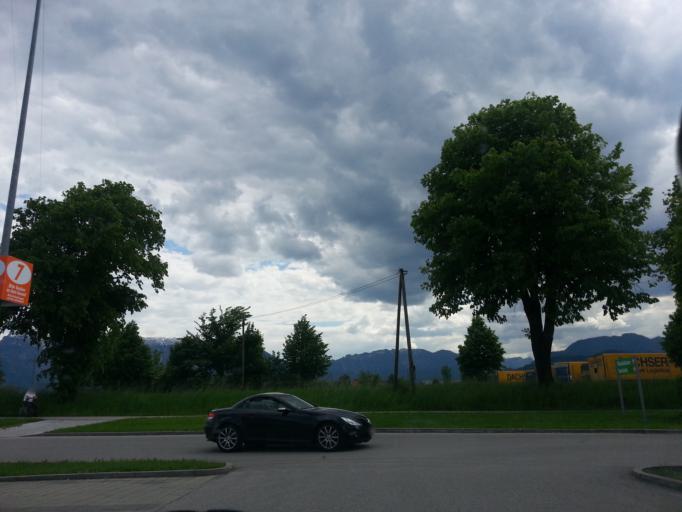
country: DE
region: Bavaria
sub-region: Upper Bavaria
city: Ainring
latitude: 47.8254
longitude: 12.9614
